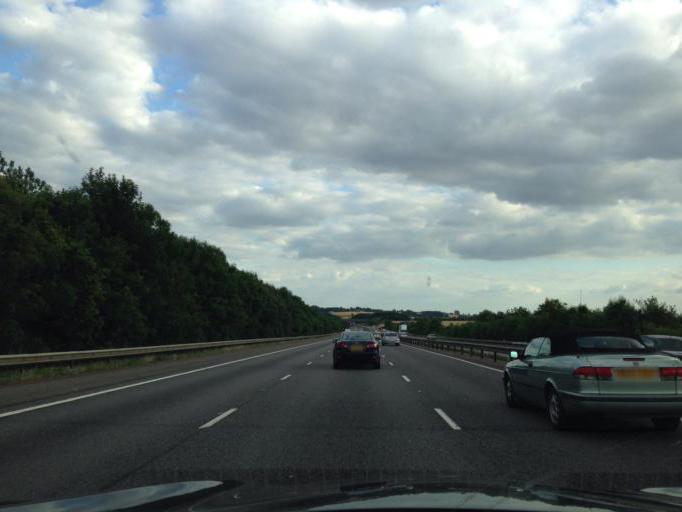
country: GB
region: England
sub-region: Oxfordshire
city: Somerton
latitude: 51.9882
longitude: -1.2664
